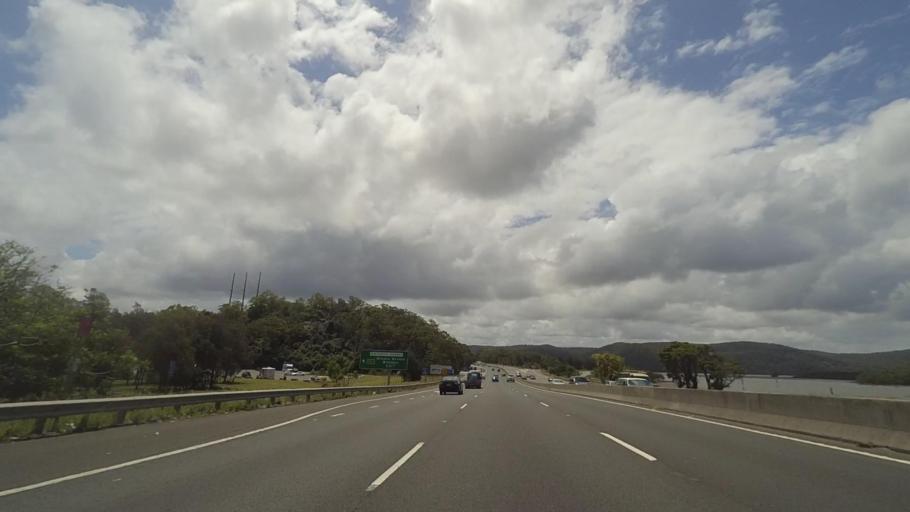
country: AU
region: New South Wales
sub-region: Hornsby Shire
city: Berowra
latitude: -33.5358
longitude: 151.1995
